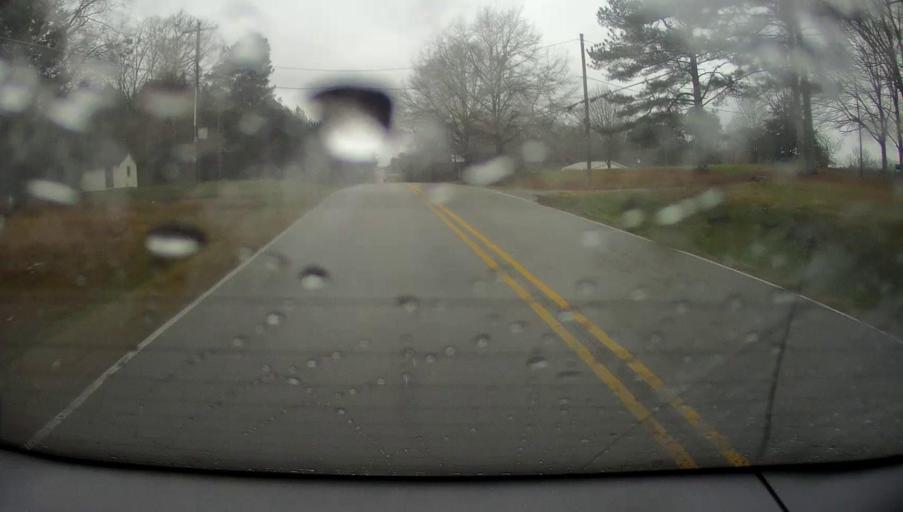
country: US
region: Alabama
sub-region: Morgan County
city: Hartselle
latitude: 34.4127
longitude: -86.9116
